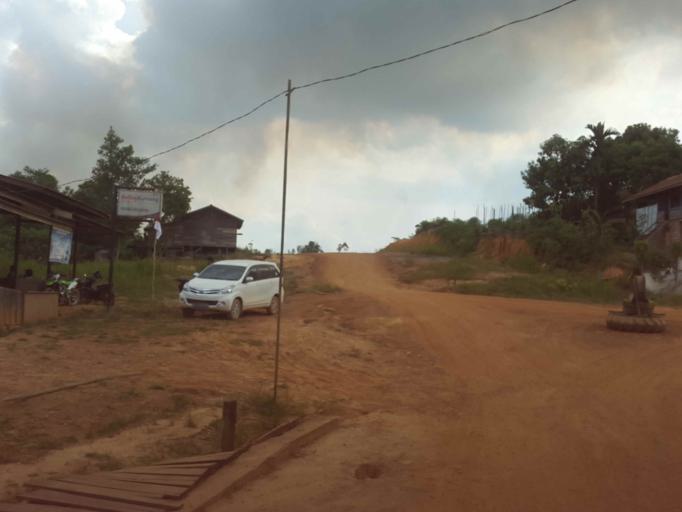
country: MY
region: Sarawak
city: Simanggang
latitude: 0.7795
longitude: 110.9900
